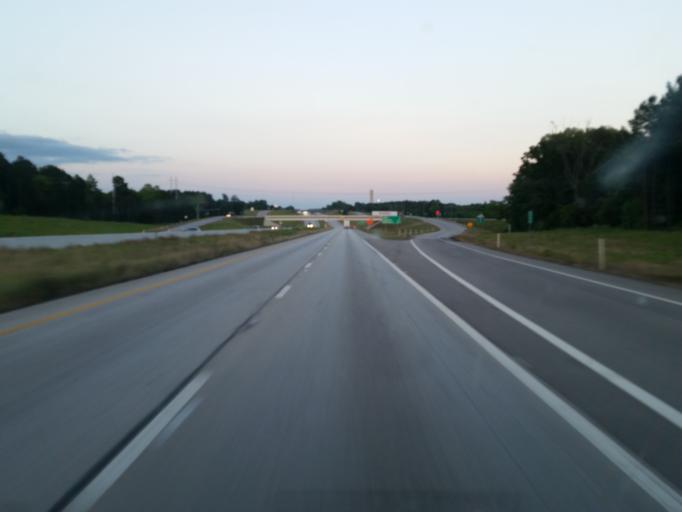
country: US
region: Texas
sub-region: Smith County
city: Hideaway
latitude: 32.4693
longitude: -95.4423
